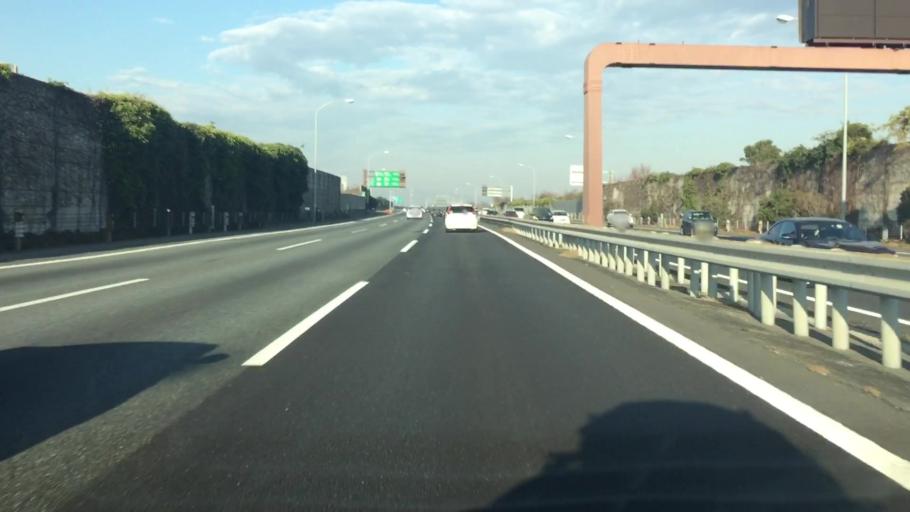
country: JP
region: Saitama
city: Sakado
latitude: 35.9494
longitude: 139.3939
